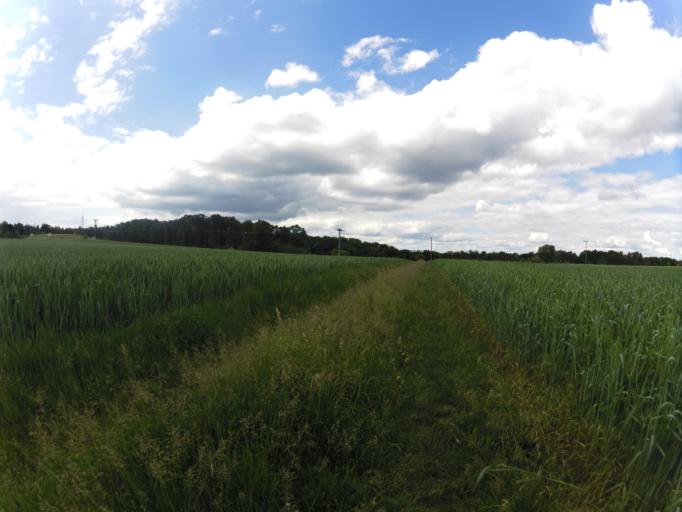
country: DE
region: Bavaria
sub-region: Regierungsbezirk Unterfranken
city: Thungersheim
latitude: 49.8781
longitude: 9.8760
